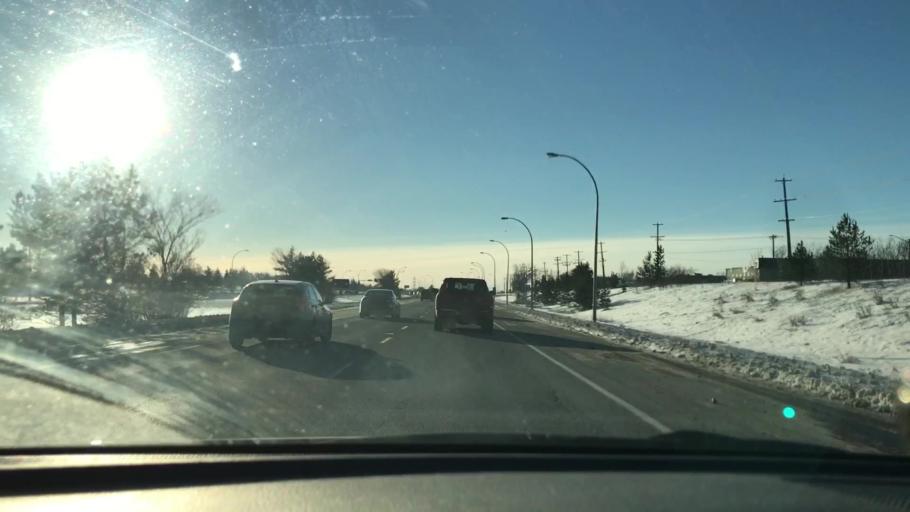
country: CA
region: Alberta
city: Edmonton
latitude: 53.4778
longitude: -113.4669
